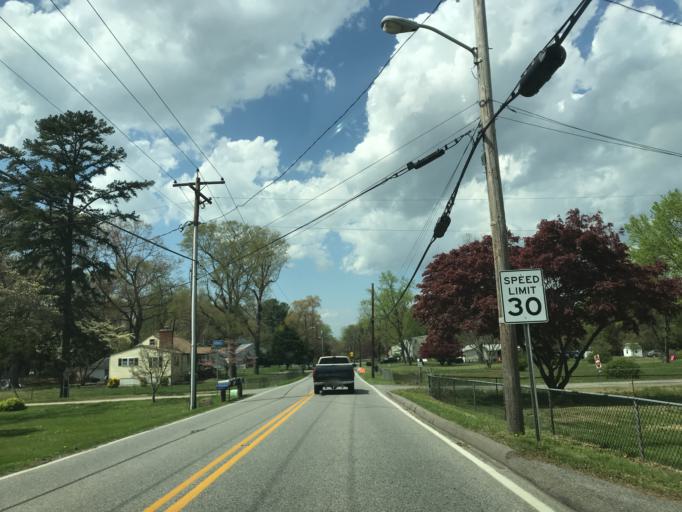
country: US
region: Maryland
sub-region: Anne Arundel County
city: Odenton
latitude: 39.0966
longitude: -76.6824
